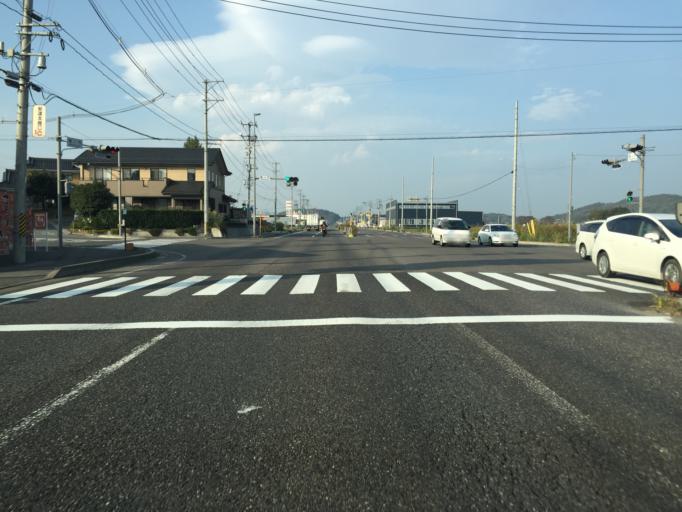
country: JP
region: Fukushima
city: Motomiya
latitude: 37.5296
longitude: 140.3962
